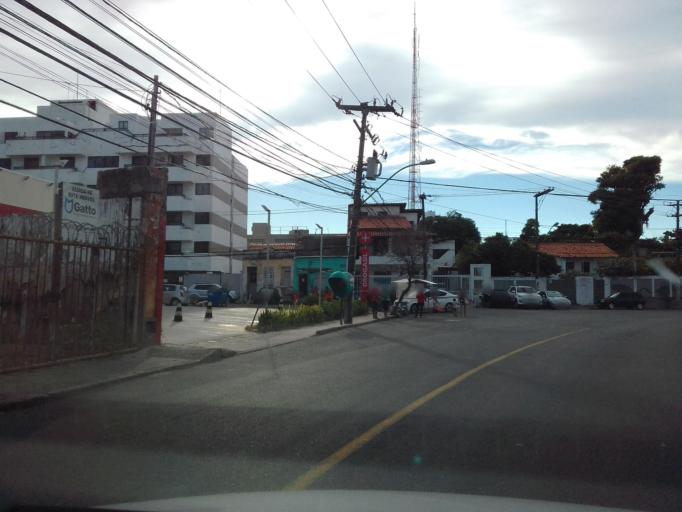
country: BR
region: Bahia
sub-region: Salvador
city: Salvador
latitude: -13.0050
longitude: -38.4987
